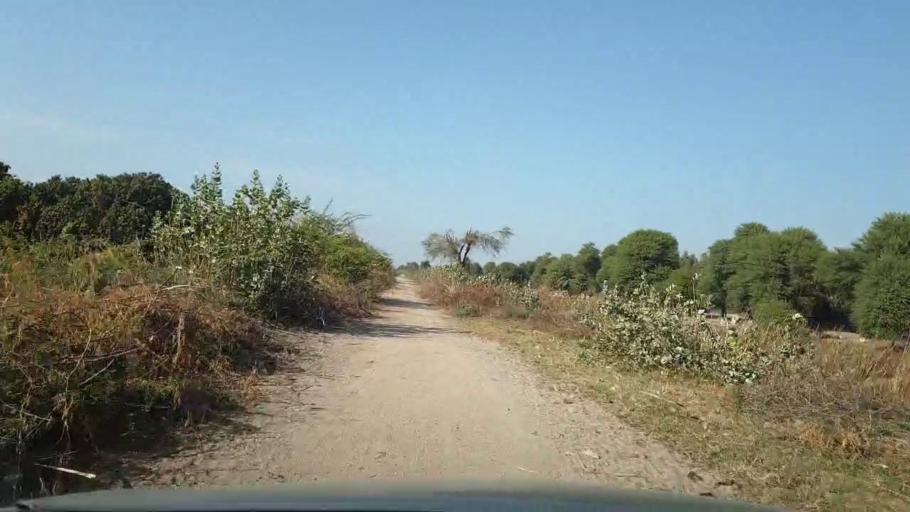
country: PK
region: Sindh
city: Tando Adam
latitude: 25.6048
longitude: 68.6245
